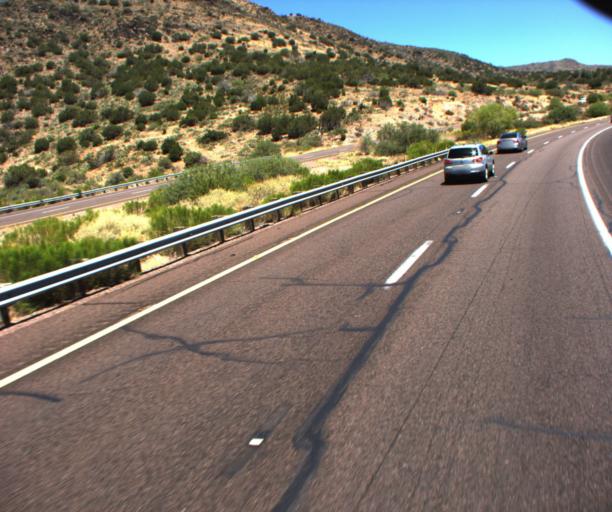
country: US
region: Arizona
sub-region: Gila County
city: Tonto Basin
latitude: 33.9800
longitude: -111.3858
